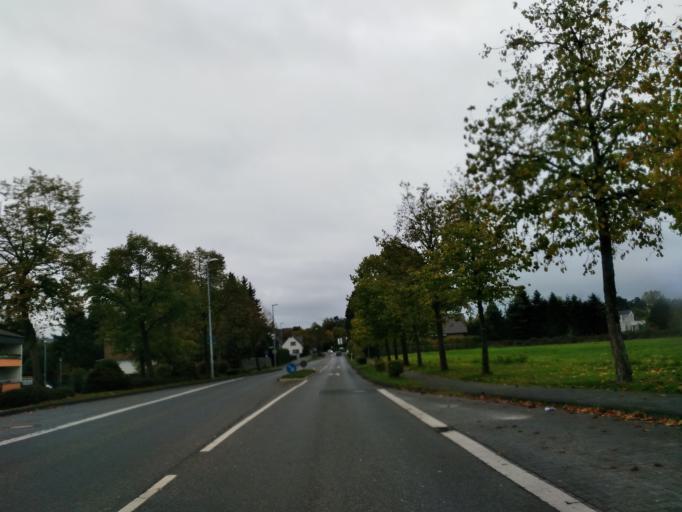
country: DE
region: Rheinland-Pfalz
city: Windhagen
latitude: 50.6565
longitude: 7.3019
